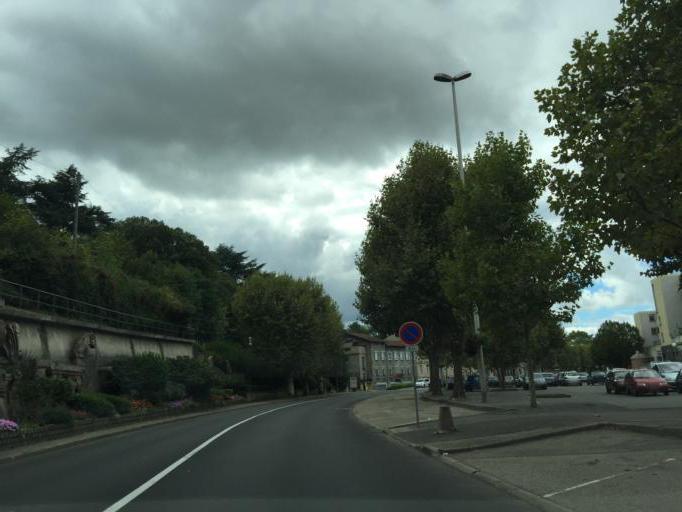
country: FR
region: Rhone-Alpes
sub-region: Departement de la Loire
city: Rive-de-Gier
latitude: 45.5297
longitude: 4.6217
